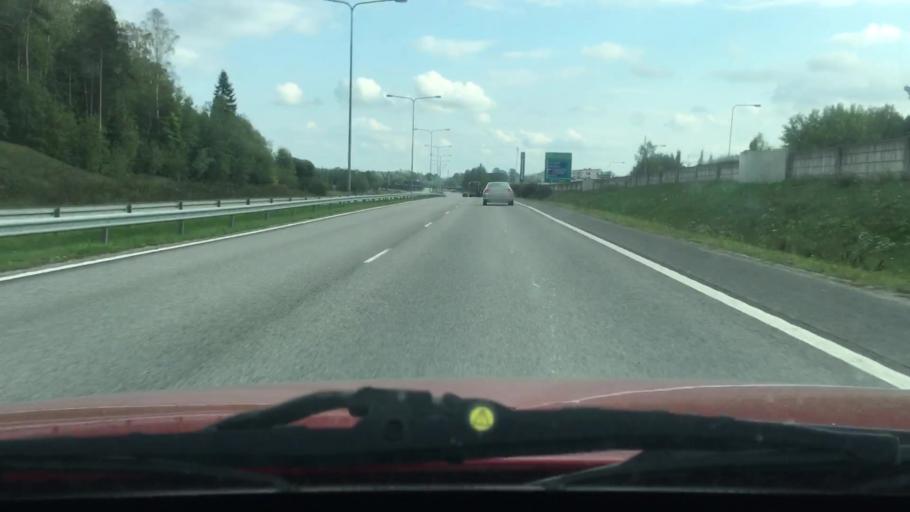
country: FI
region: Varsinais-Suomi
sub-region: Turku
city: Raisio
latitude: 60.4946
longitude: 22.1666
